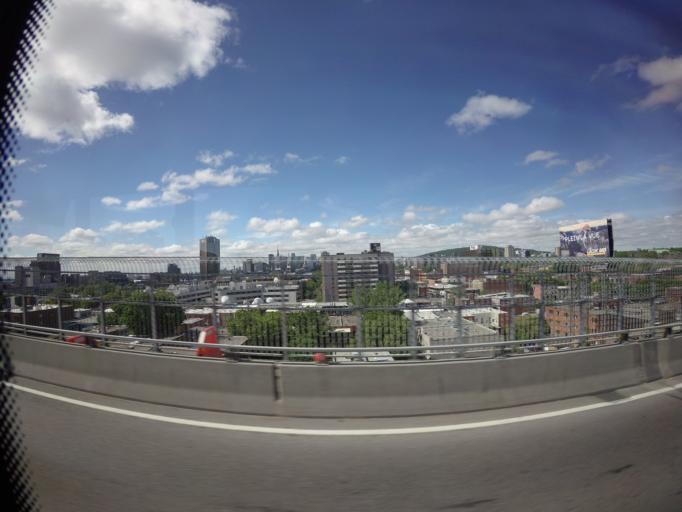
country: CA
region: Quebec
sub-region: Monteregie
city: Longueuil
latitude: 45.5239
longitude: -73.5496
